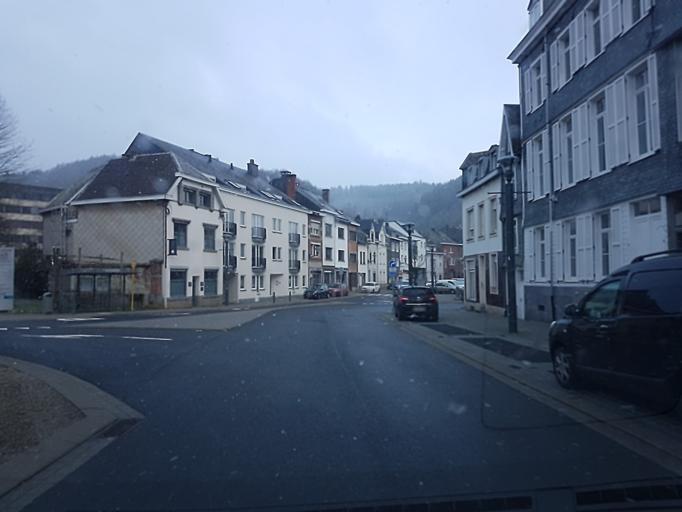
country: BE
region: Wallonia
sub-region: Province de Liege
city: Malmedy
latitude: 50.4262
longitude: 6.0257
